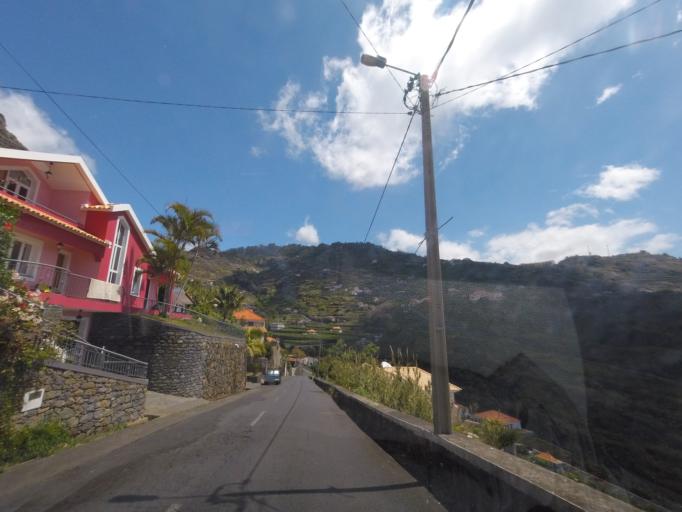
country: PT
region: Madeira
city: Ponta do Sol
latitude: 32.6809
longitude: -17.0786
